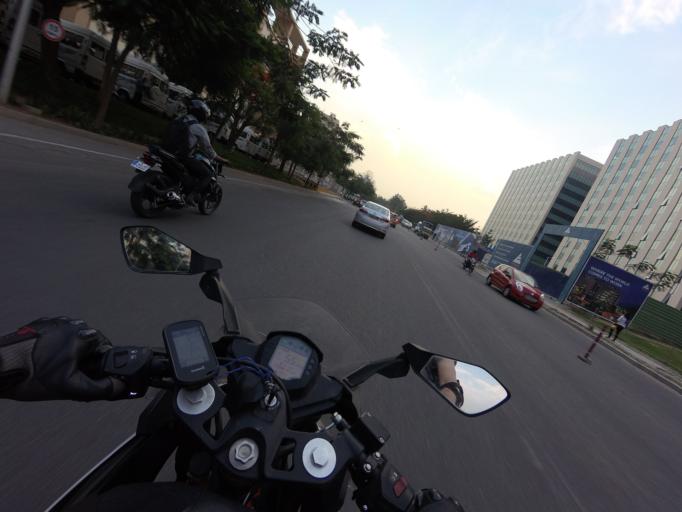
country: IN
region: Karnataka
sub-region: Bangalore Urban
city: Yelahanka
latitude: 13.0451
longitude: 77.6196
